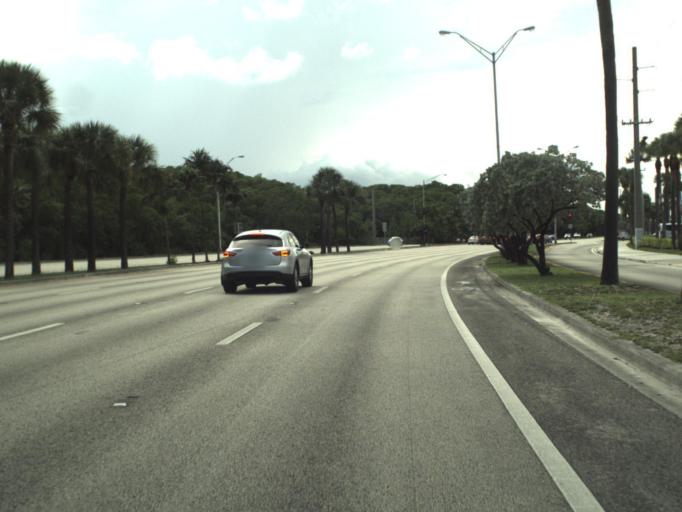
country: US
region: Florida
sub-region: Miami-Dade County
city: North Miami Beach
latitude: 25.9268
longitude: -80.1389
